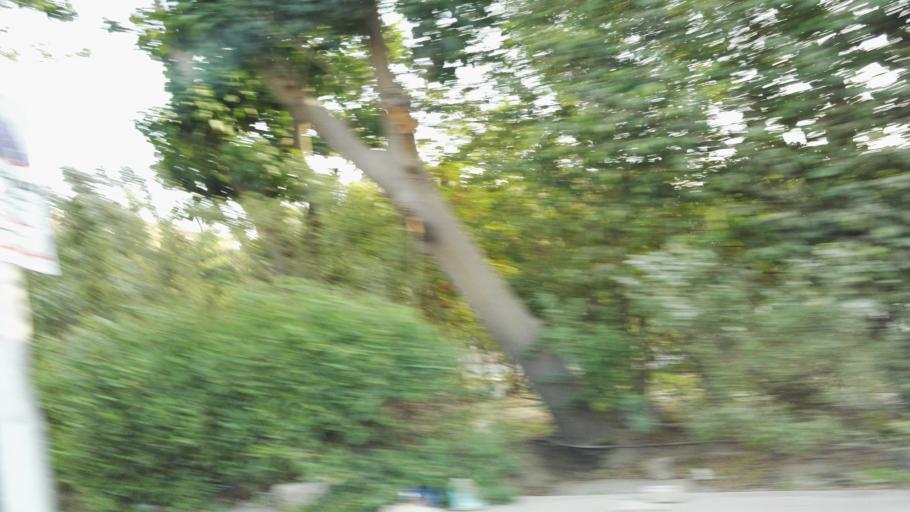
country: EG
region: Muhafazat al Qahirah
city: Cairo
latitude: 29.9982
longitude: 31.4068
